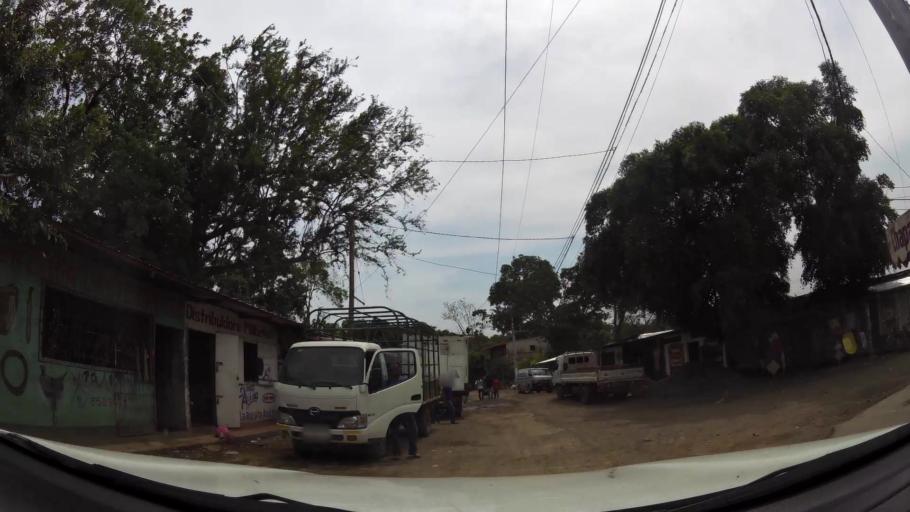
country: NI
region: Rivas
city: Rivas
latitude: 11.4400
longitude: -85.8330
